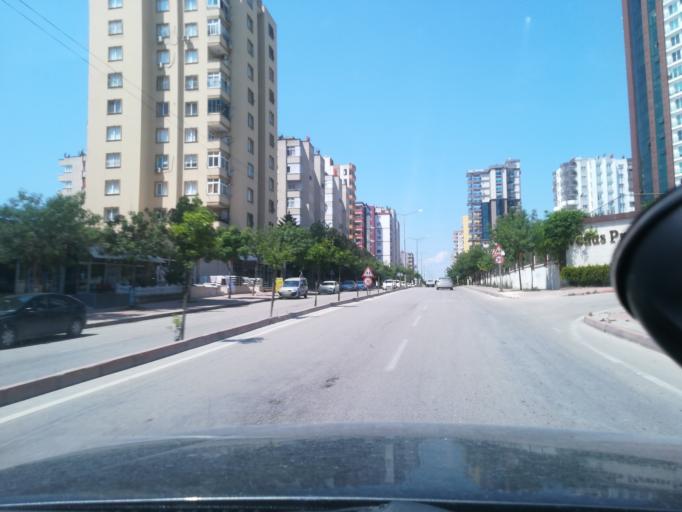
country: TR
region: Adana
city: Seyhan
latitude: 37.0344
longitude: 35.2649
